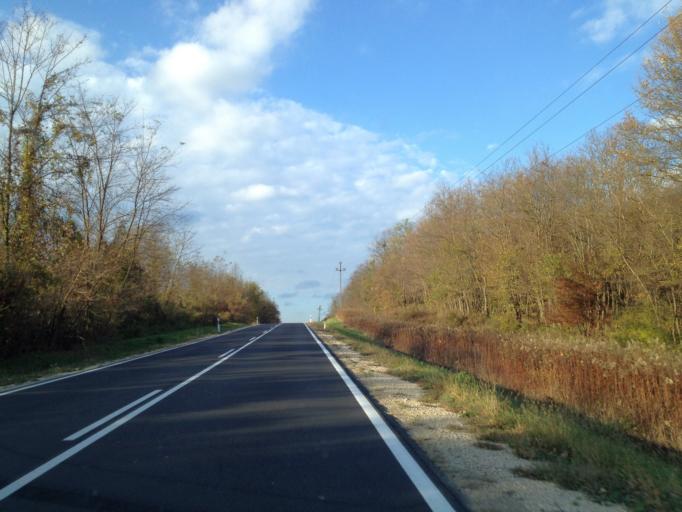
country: HU
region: Gyor-Moson-Sopron
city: Bakonyszentlaszlo
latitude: 47.4089
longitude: 17.8524
